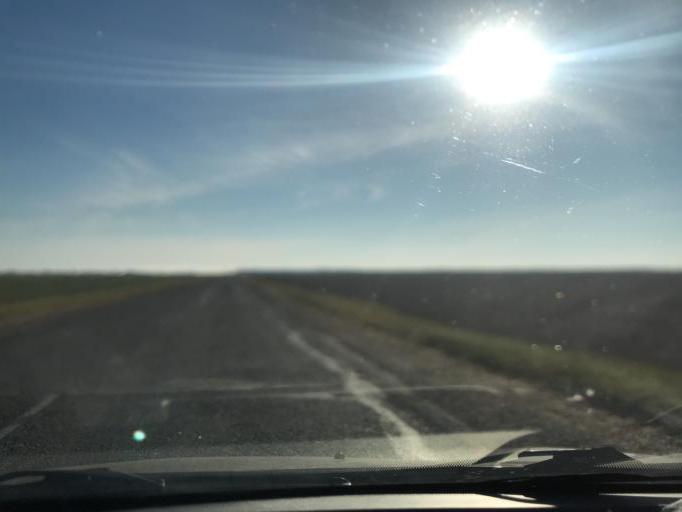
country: BY
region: Gomel
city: Brahin
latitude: 51.7914
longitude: 30.1738
